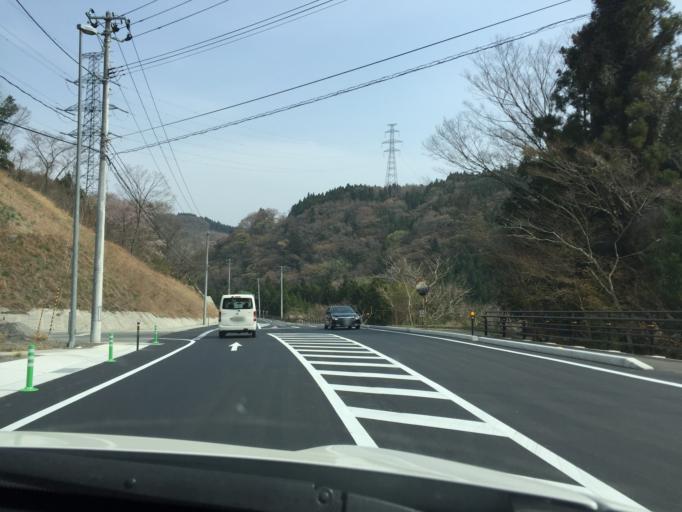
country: JP
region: Fukushima
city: Iwaki
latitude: 37.0036
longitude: 140.7018
